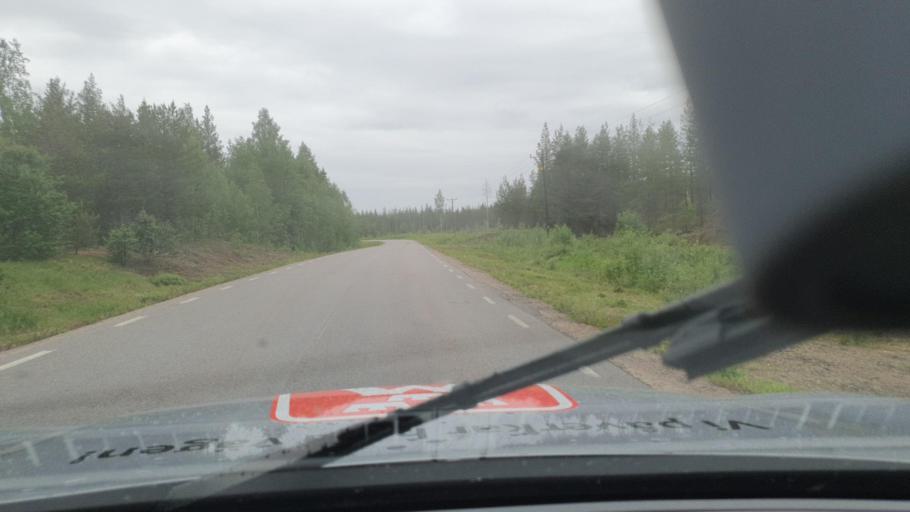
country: SE
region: Norrbotten
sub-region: Pajala Kommun
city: Pajala
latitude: 66.7726
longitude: 23.1454
